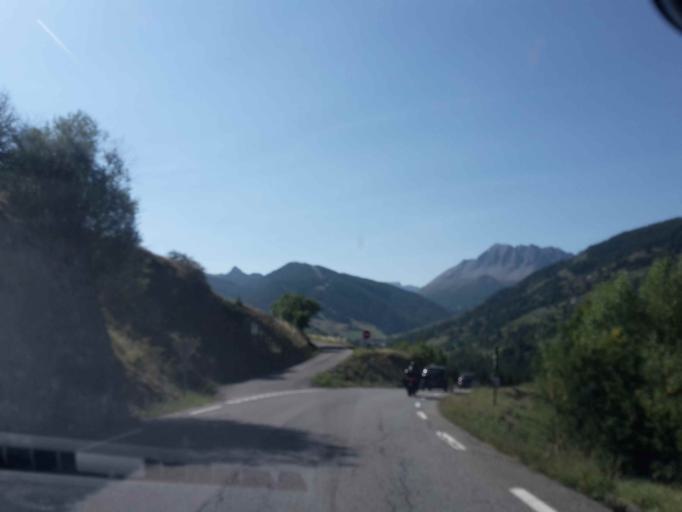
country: FR
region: Provence-Alpes-Cote d'Azur
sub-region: Departement des Hautes-Alpes
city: Guillestre
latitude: 44.6157
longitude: 6.6858
